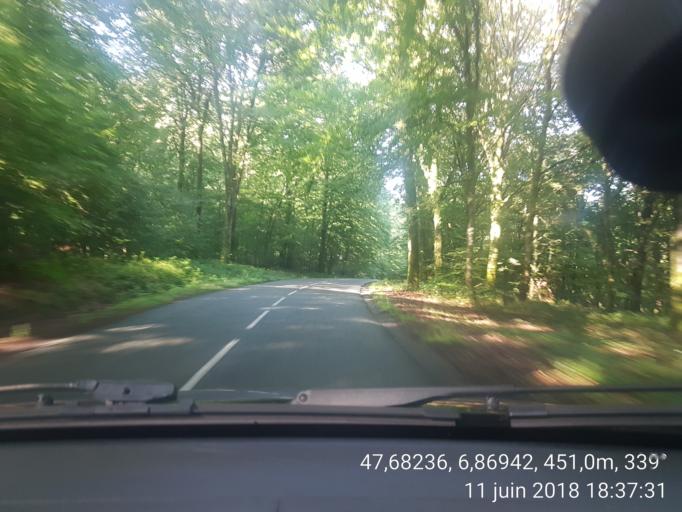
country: FR
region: Franche-Comte
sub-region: Territoire de Belfort
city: Offemont
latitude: 47.6822
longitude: 6.8692
